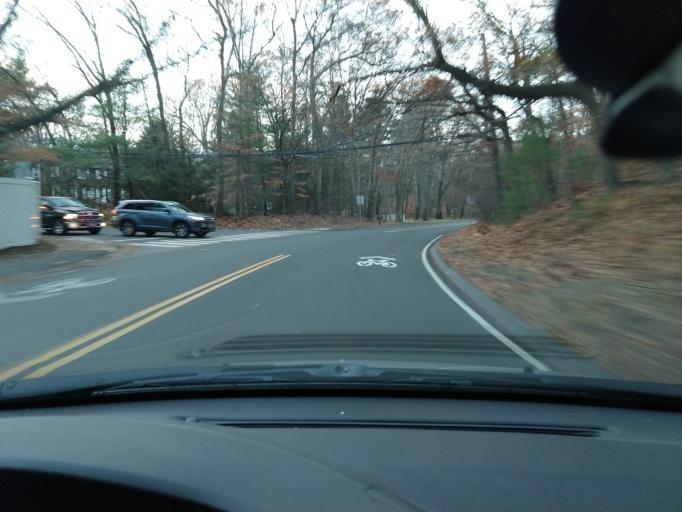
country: US
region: Massachusetts
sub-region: Middlesex County
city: Lexington
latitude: 42.4770
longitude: -71.2403
